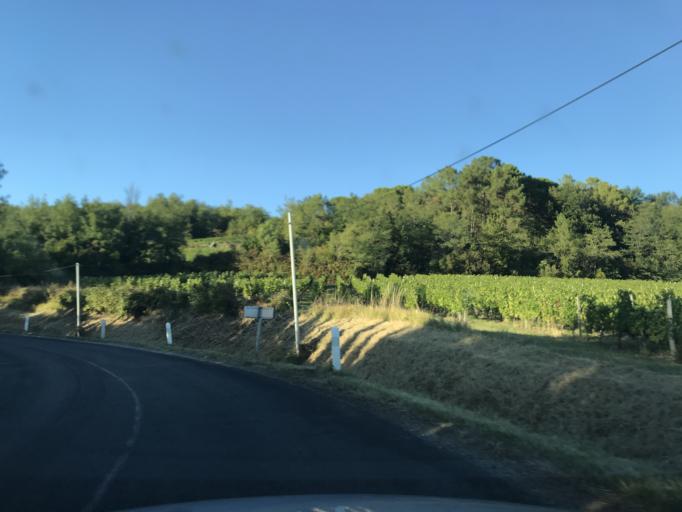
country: FR
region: Aquitaine
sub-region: Departement de la Gironde
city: Mouliets-et-Villemartin
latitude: 44.8770
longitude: -0.0457
